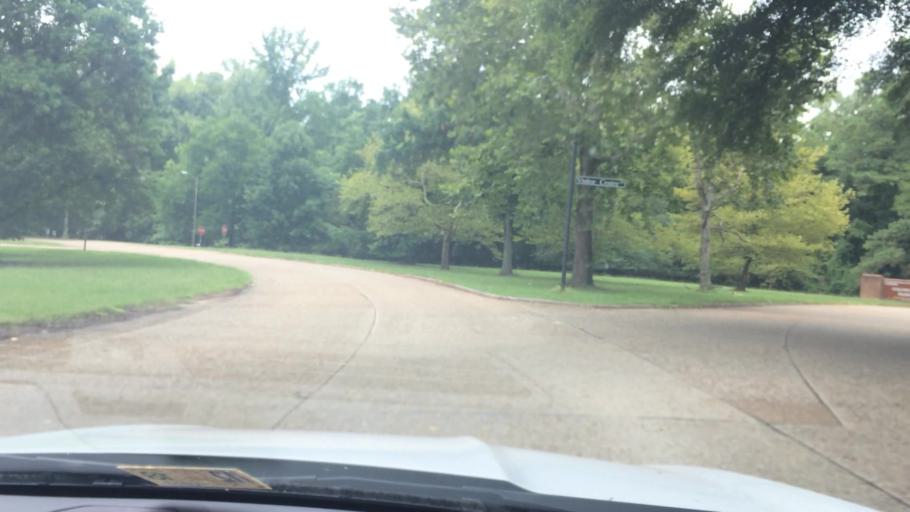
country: US
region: Virginia
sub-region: City of Williamsburg
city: Williamsburg
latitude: 37.2774
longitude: -76.6982
